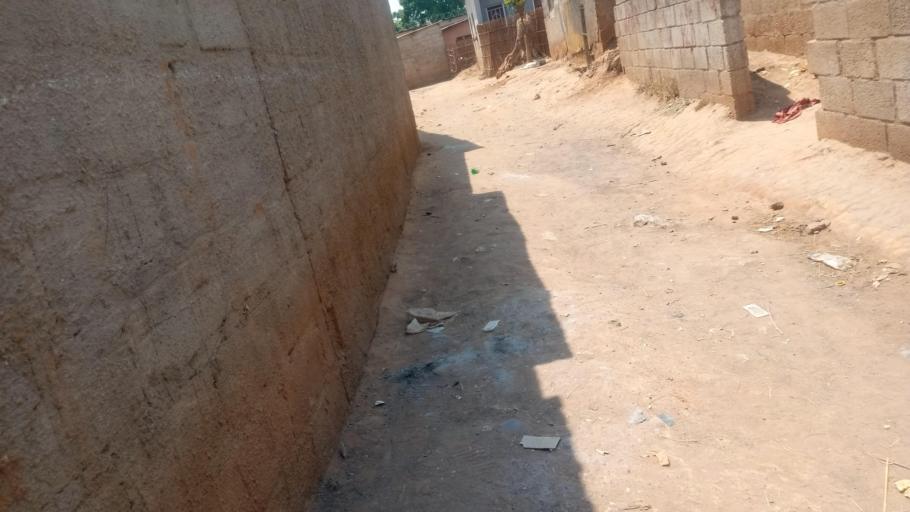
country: ZM
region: Lusaka
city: Lusaka
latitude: -15.4445
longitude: 28.3834
